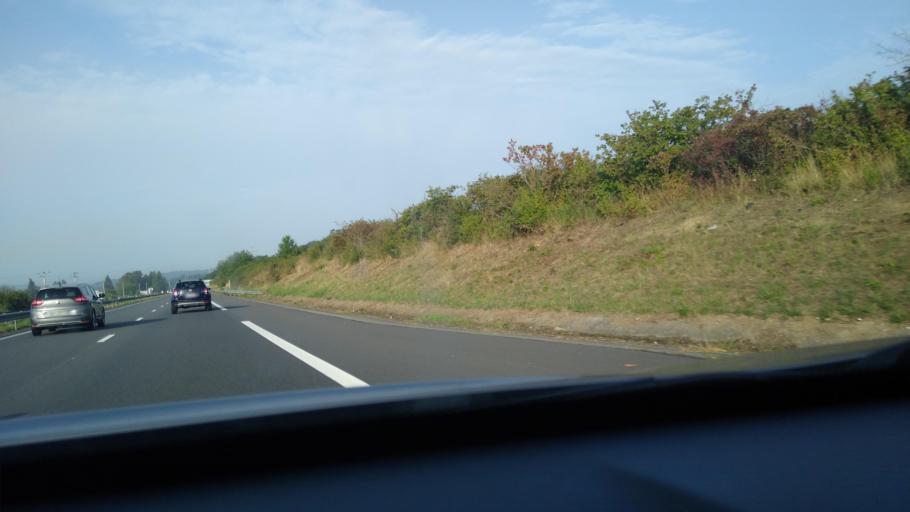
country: FR
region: Midi-Pyrenees
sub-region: Departement de la Haute-Garonne
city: Martres-Tolosane
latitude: 43.1972
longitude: 0.9969
